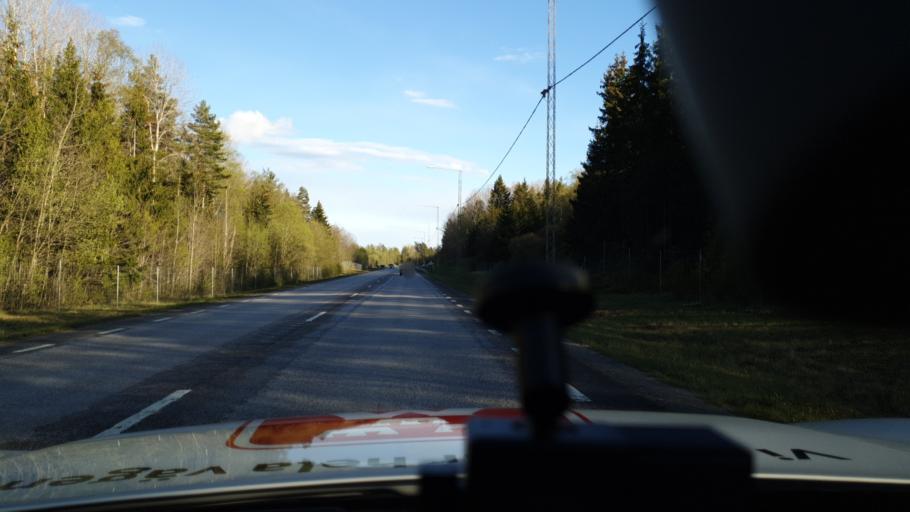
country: SE
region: Stockholm
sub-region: Vallentuna Kommun
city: Vallentuna
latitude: 59.4855
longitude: 18.1131
